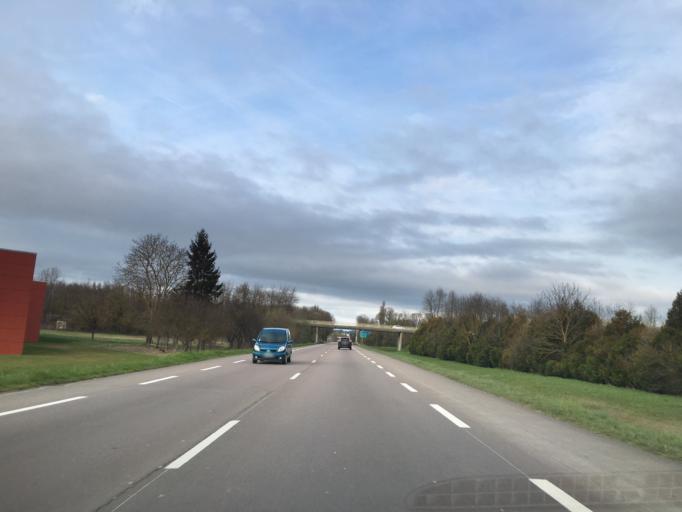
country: FR
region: Bourgogne
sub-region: Departement de l'Yonne
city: Maillot
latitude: 48.1780
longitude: 3.2979
